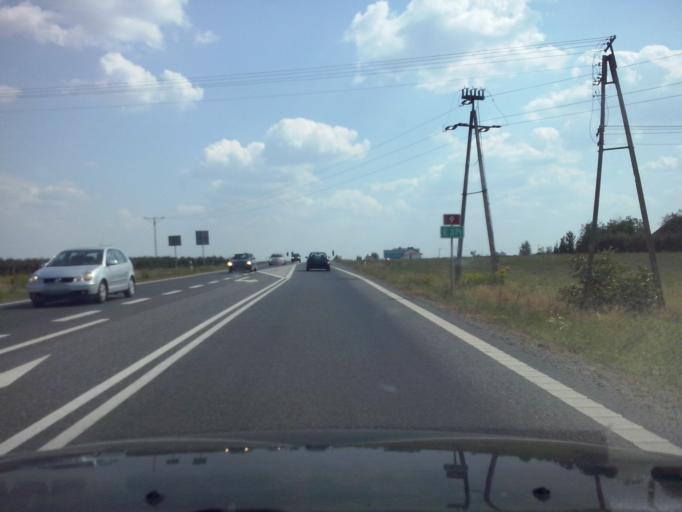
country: PL
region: Swietokrzyskie
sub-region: Powiat sandomierski
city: Loniow
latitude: 50.5564
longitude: 21.5311
